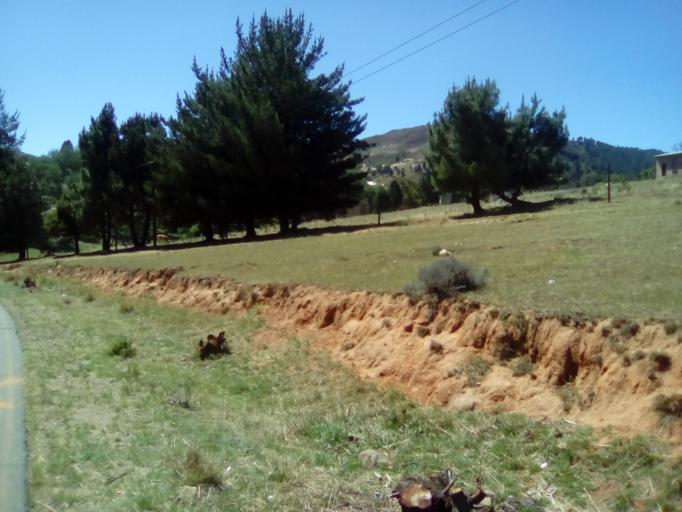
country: LS
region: Qacha's Nek
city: Qacha's Nek
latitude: -30.1169
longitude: 28.6864
